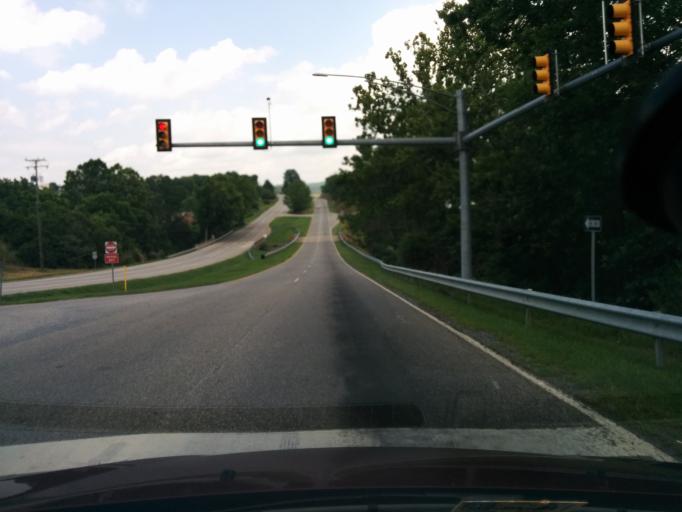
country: US
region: Virginia
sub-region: Rockbridge County
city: East Lexington
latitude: 37.8039
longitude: -79.4079
